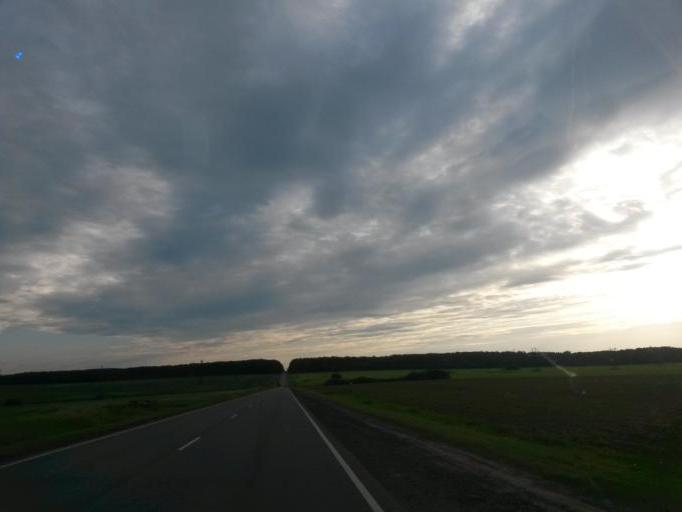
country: RU
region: Moskovskaya
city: Barybino
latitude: 55.2032
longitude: 37.8649
